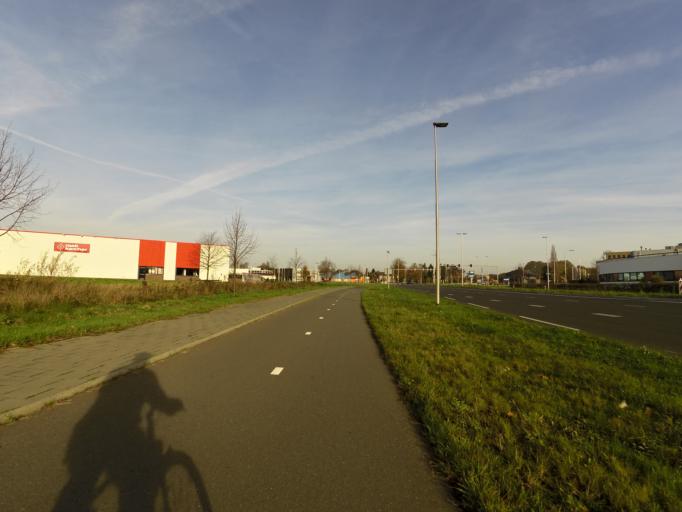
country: NL
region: Gelderland
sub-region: Gemeente Doetinchem
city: Doetinchem
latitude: 51.9541
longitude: 6.2992
